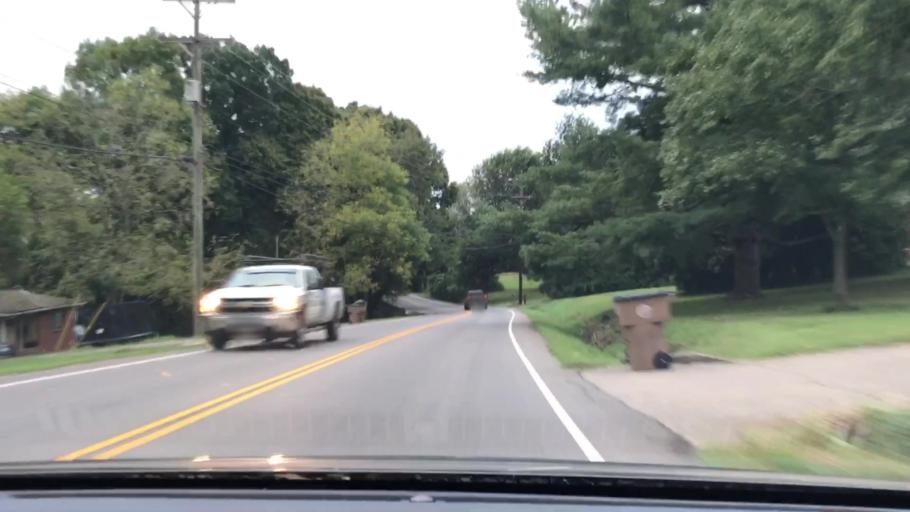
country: US
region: Tennessee
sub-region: Davidson County
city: Oak Hill
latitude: 36.0683
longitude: -86.7069
